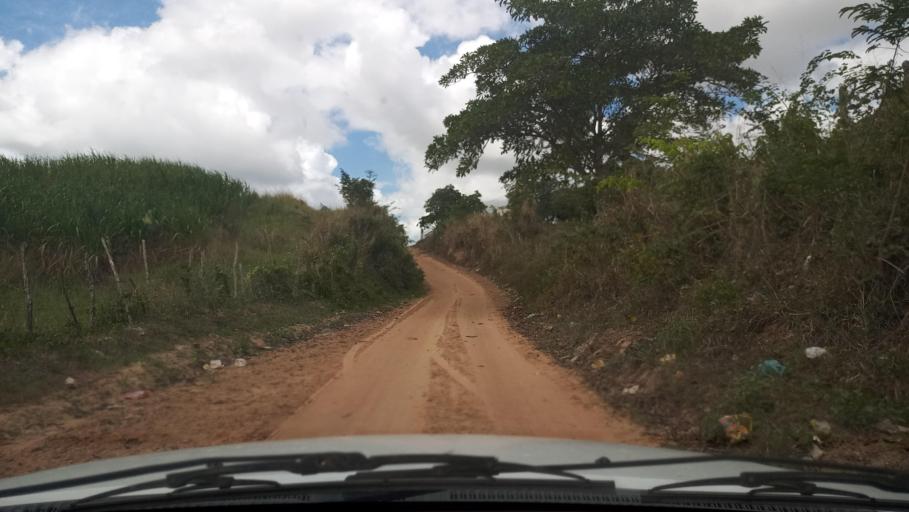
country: BR
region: Rio Grande do Norte
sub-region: Goianinha
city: Goianinha
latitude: -6.2641
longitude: -35.2380
